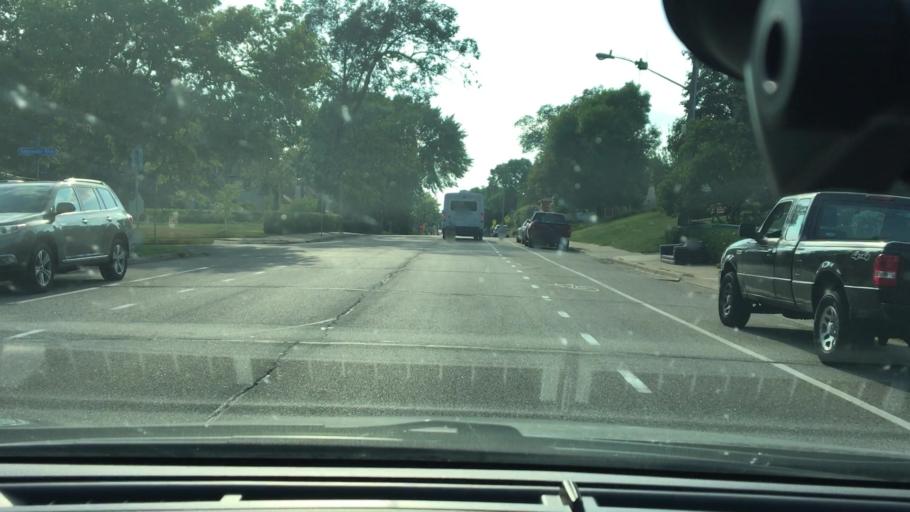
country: US
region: Minnesota
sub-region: Hennepin County
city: Richfield
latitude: 44.9053
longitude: -93.2540
